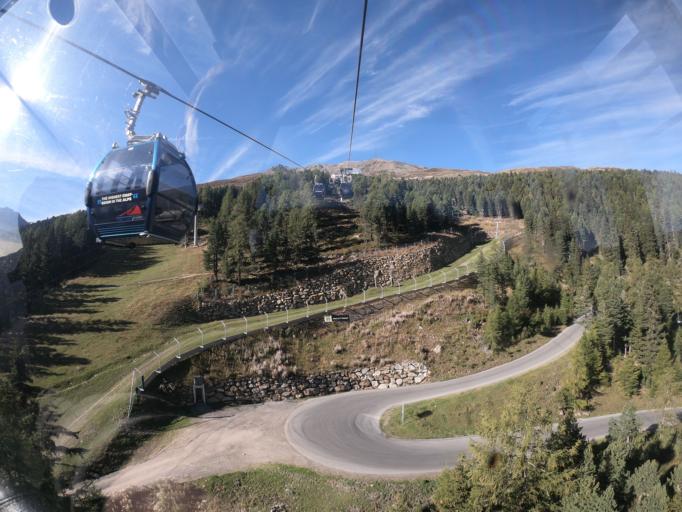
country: AT
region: Tyrol
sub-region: Politischer Bezirk Imst
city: Soelden
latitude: 46.9544
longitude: 10.9960
